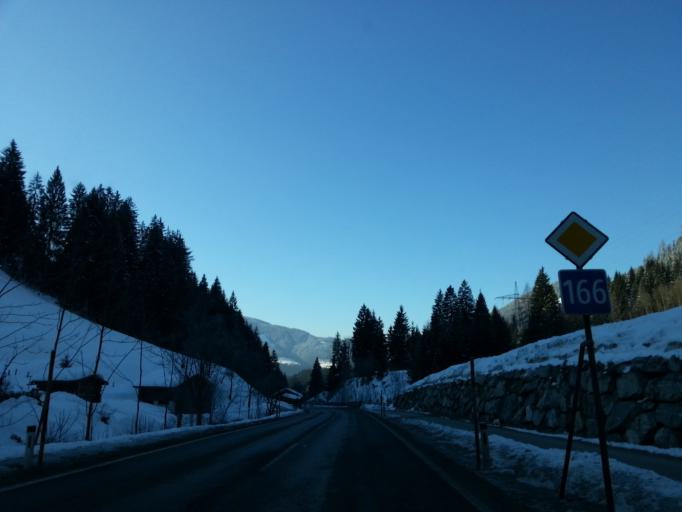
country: AT
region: Salzburg
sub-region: Politischer Bezirk Sankt Johann im Pongau
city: Eben im Pongau
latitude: 47.4550
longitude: 13.3695
